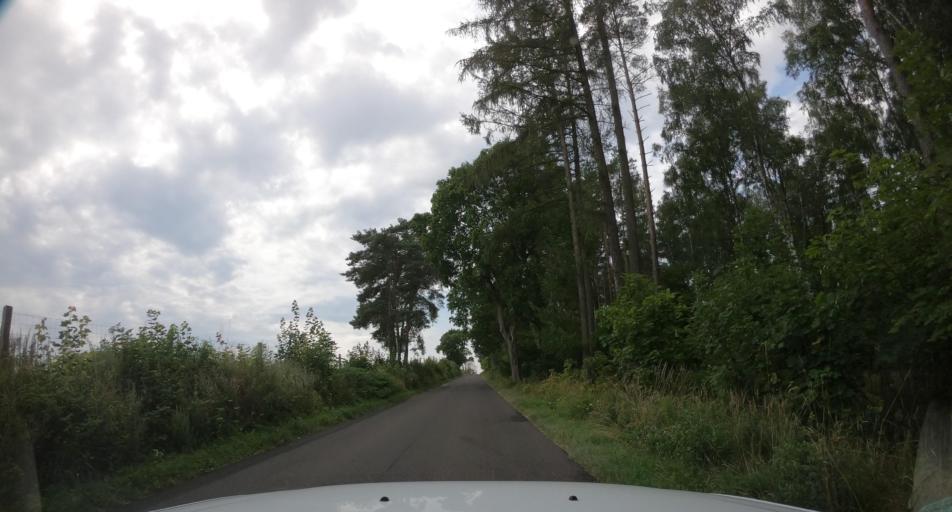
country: PL
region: West Pomeranian Voivodeship
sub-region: Powiat walecki
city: Walcz
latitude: 53.2350
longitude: 16.3289
